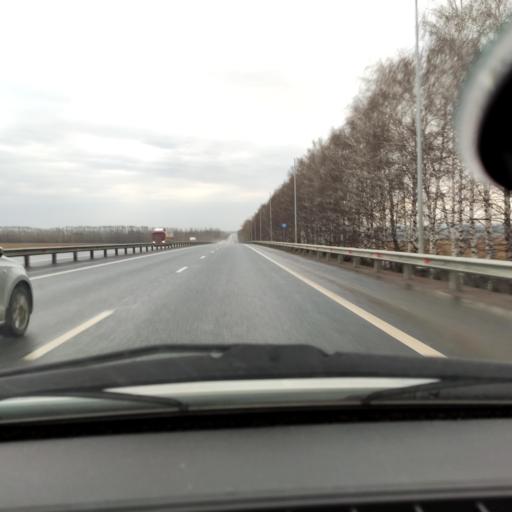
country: RU
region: Bashkortostan
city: Karmaskaly
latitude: 54.3465
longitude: 55.9062
